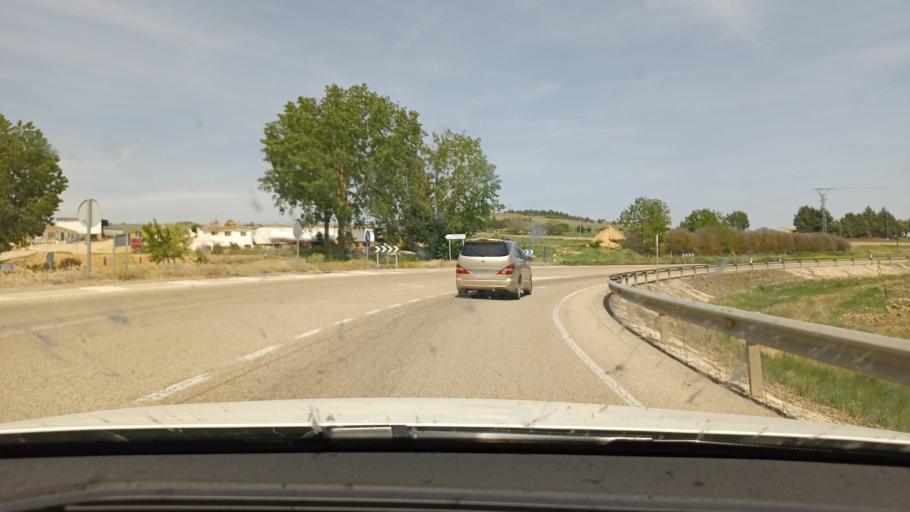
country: ES
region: Castille and Leon
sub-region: Provincia de Soria
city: Almazan
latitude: 41.4762
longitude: -2.5514
